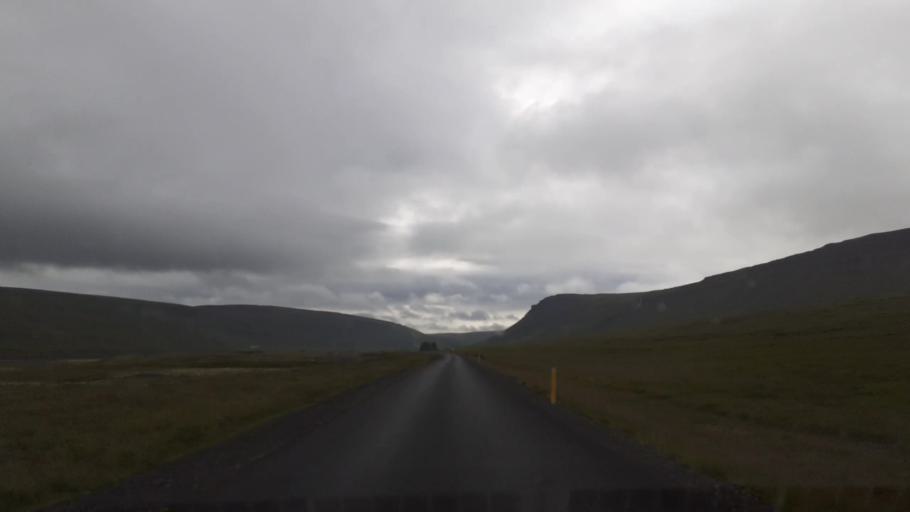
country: IS
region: East
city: Egilsstadir
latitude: 65.6246
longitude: -15.0810
